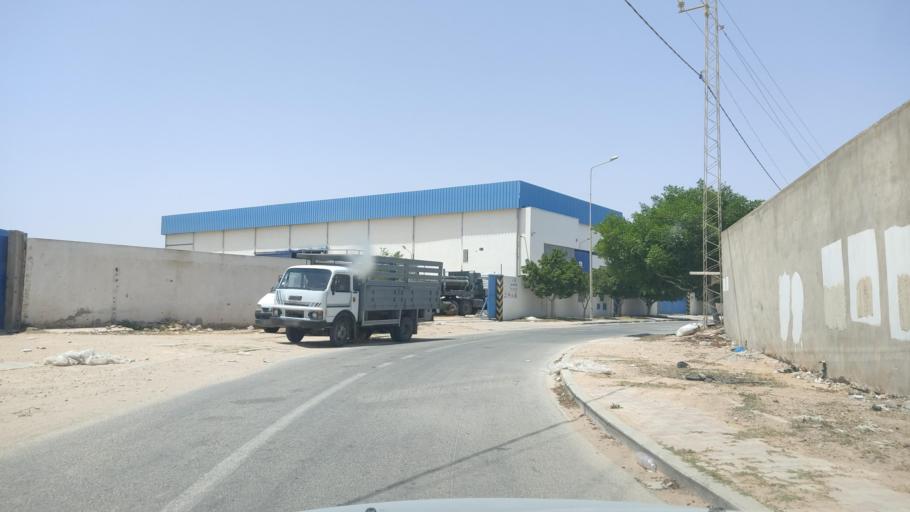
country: TN
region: Safaqis
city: Sfax
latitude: 34.6596
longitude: 10.6973
